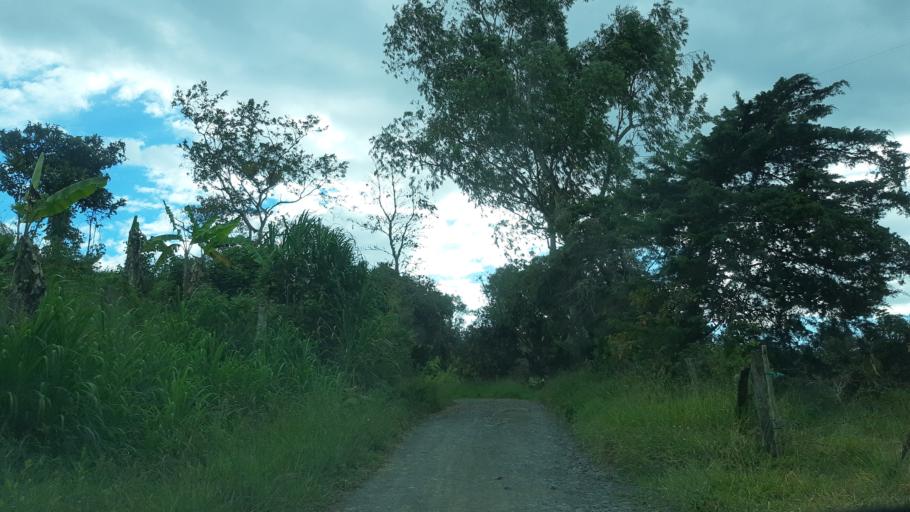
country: CO
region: Boyaca
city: Garagoa
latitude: 5.0203
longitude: -73.3323
